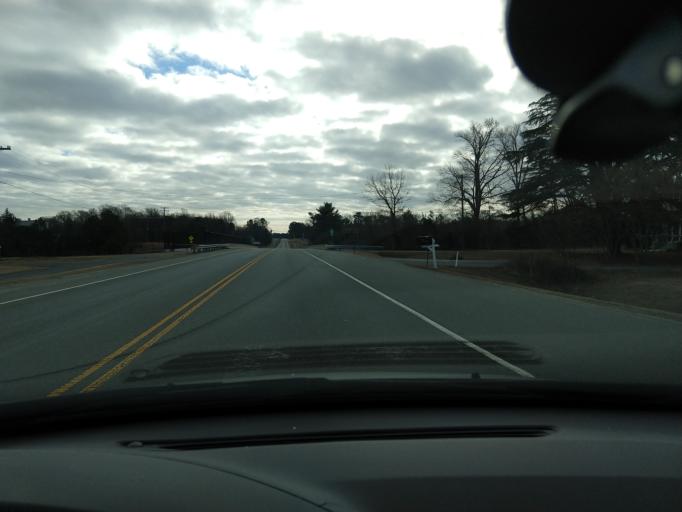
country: US
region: Virginia
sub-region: Henrico County
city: Fort Lee
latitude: 37.4623
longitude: -77.3799
